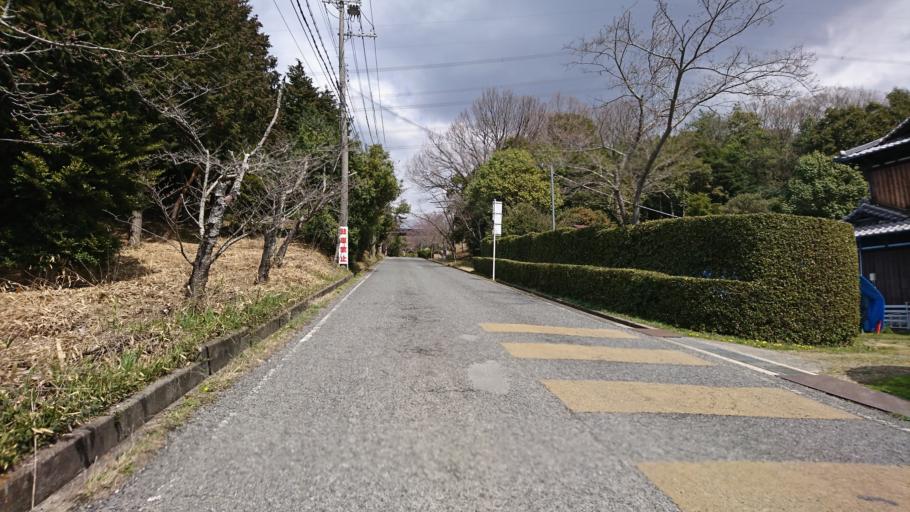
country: JP
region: Hyogo
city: Miki
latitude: 34.7714
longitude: 134.9476
